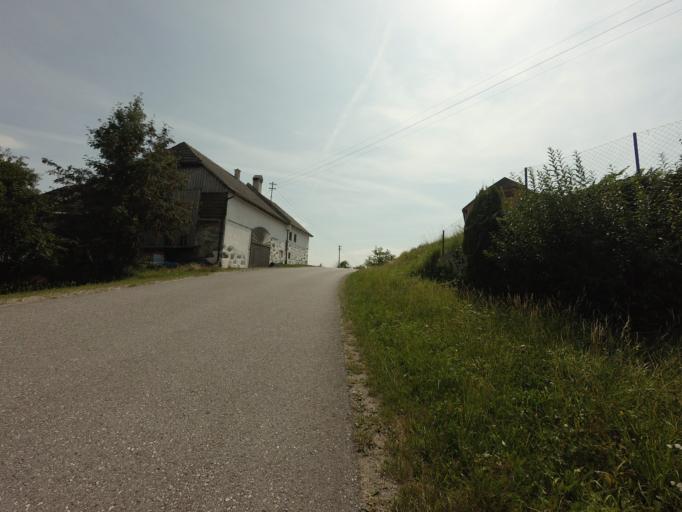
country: AT
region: Upper Austria
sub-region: Politischer Bezirk Urfahr-Umgebung
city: Schenkenfelden
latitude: 48.5253
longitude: 14.3611
